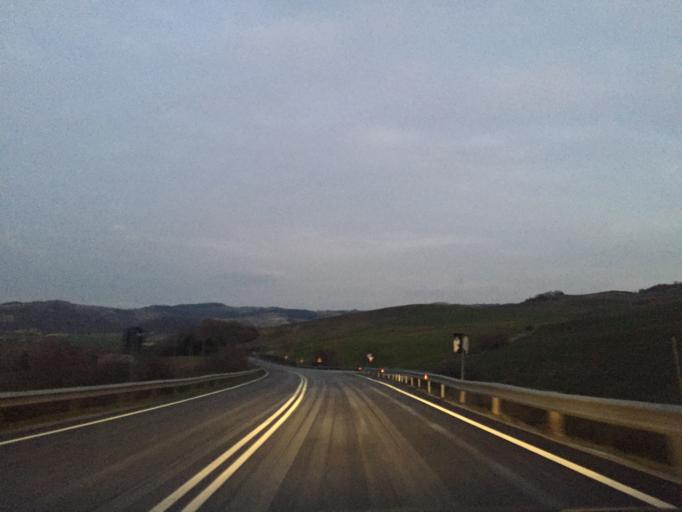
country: IT
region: Apulia
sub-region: Provincia di Foggia
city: Volturara Appula
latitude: 41.4573
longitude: 15.0632
